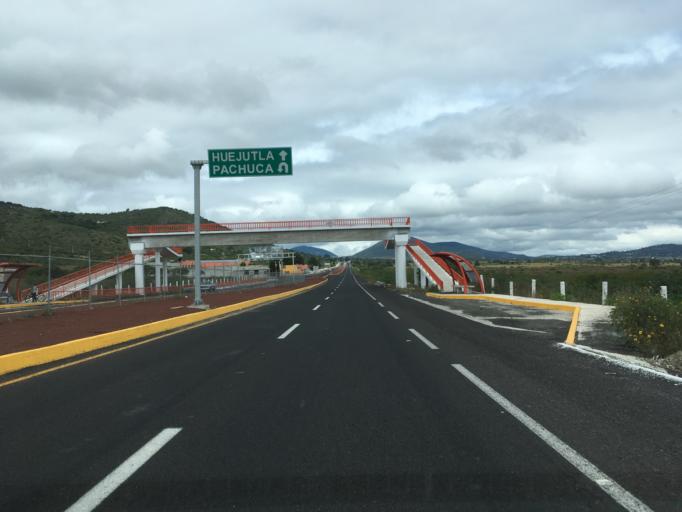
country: MX
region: Hidalgo
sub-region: Atotonilco el Grande
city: Santa Maria Amajac
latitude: 20.3475
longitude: -98.7122
